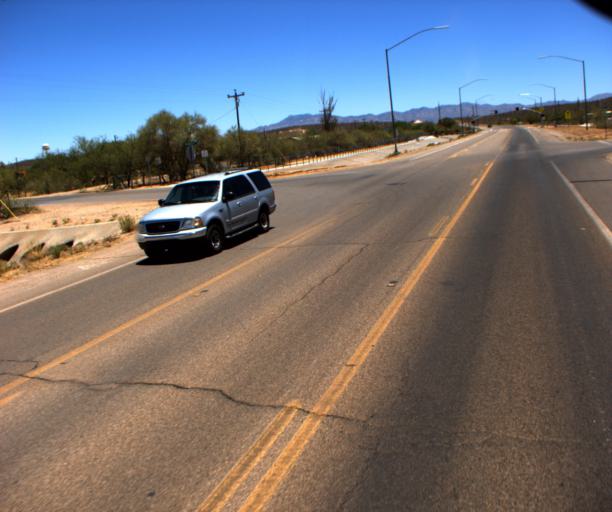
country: US
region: Arizona
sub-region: Pima County
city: Sells
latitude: 31.9163
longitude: -111.8663
